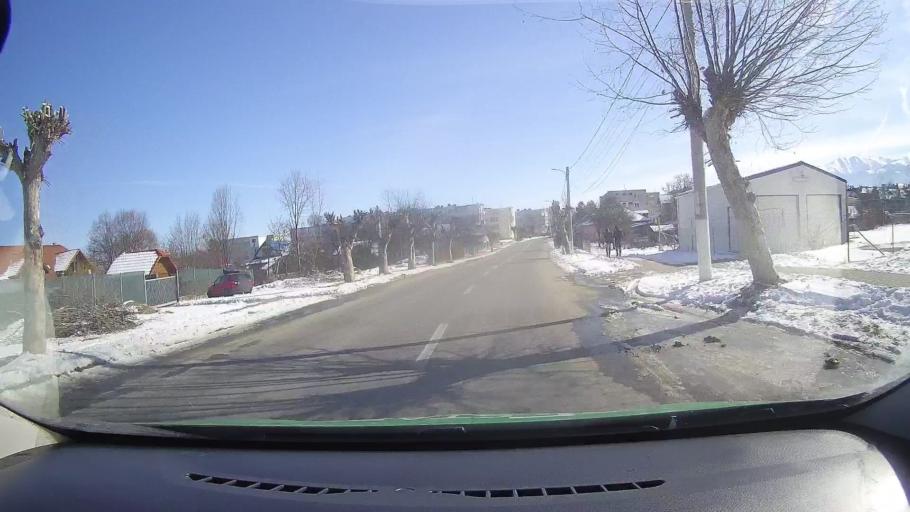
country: RO
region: Brasov
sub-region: Oras Victoria
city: Victoria
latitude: 45.7344
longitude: 24.6974
